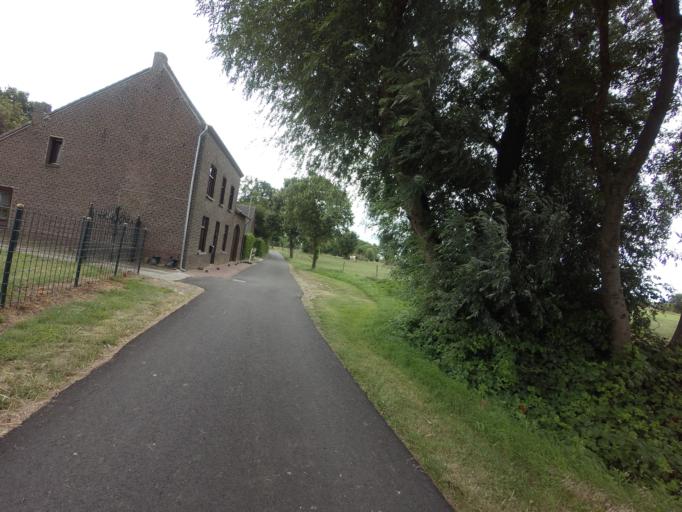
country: NL
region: Limburg
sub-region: Valkenburg aan de Geul
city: Berg
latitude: 50.8434
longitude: 5.7974
